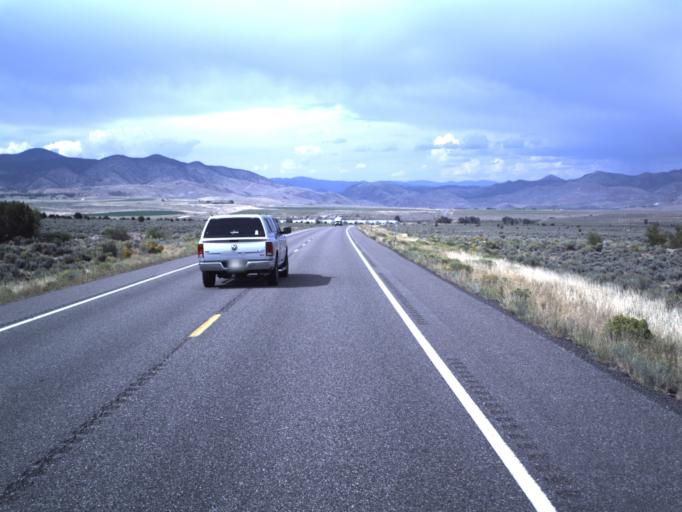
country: US
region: Utah
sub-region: Piute County
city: Junction
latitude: 38.3878
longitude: -112.2299
